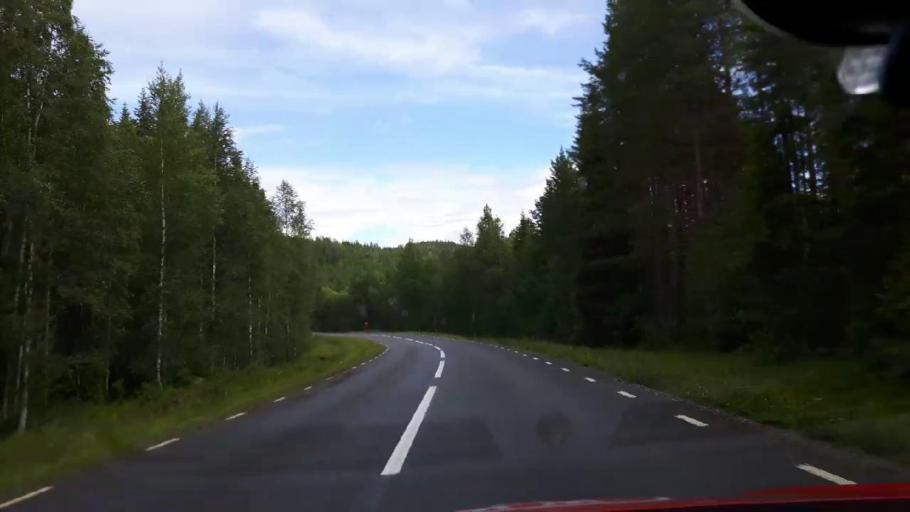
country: SE
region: Jaemtland
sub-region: Stroemsunds Kommun
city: Stroemsund
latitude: 64.3407
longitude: 14.9353
